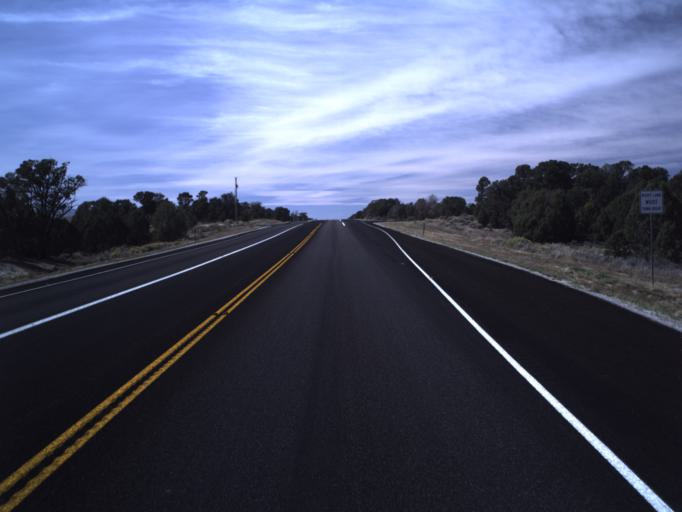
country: US
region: Colorado
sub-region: Dolores County
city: Dove Creek
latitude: 37.8220
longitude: -109.0611
